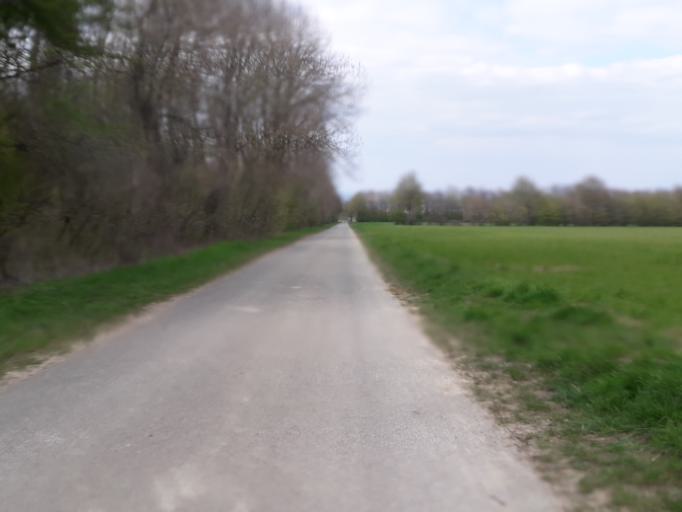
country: DE
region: North Rhine-Westphalia
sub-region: Regierungsbezirk Detmold
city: Paderborn
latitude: 51.6925
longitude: 8.7636
